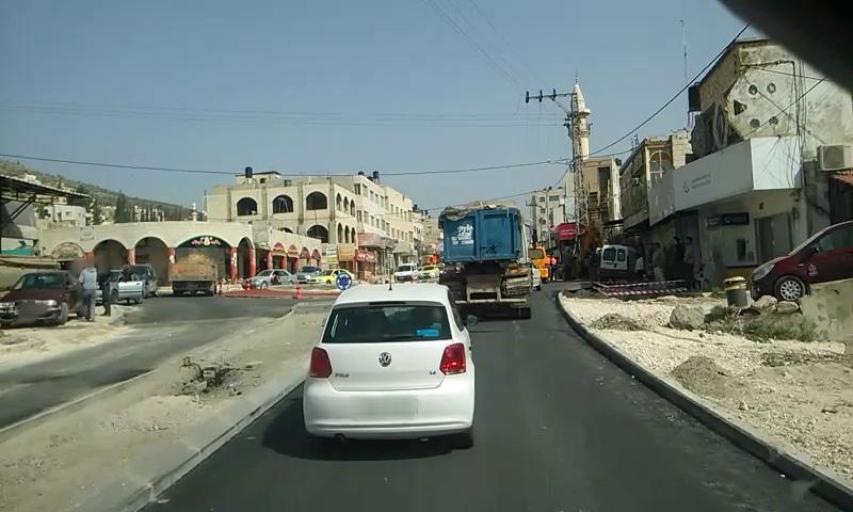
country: PS
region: West Bank
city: Huwwarah
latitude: 32.1486
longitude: 35.2579
